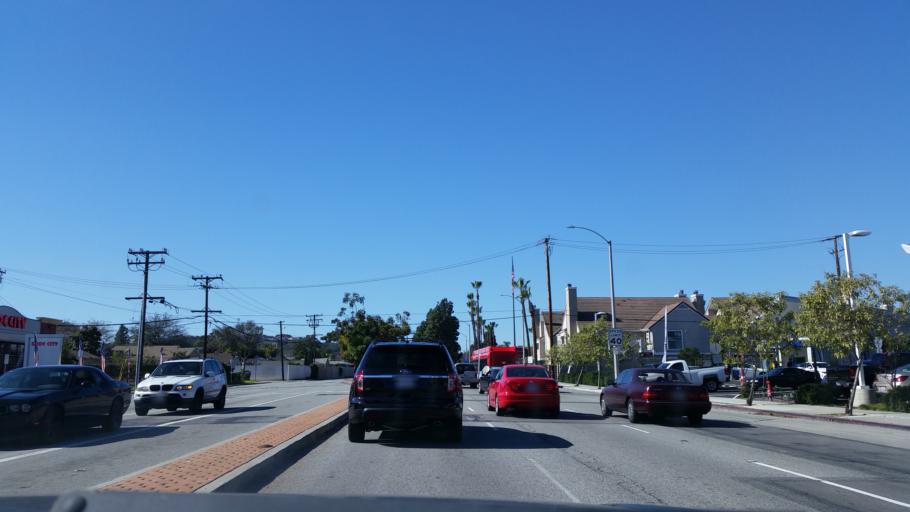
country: US
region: California
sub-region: Los Angeles County
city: Signal Hill
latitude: 33.8034
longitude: -118.1429
